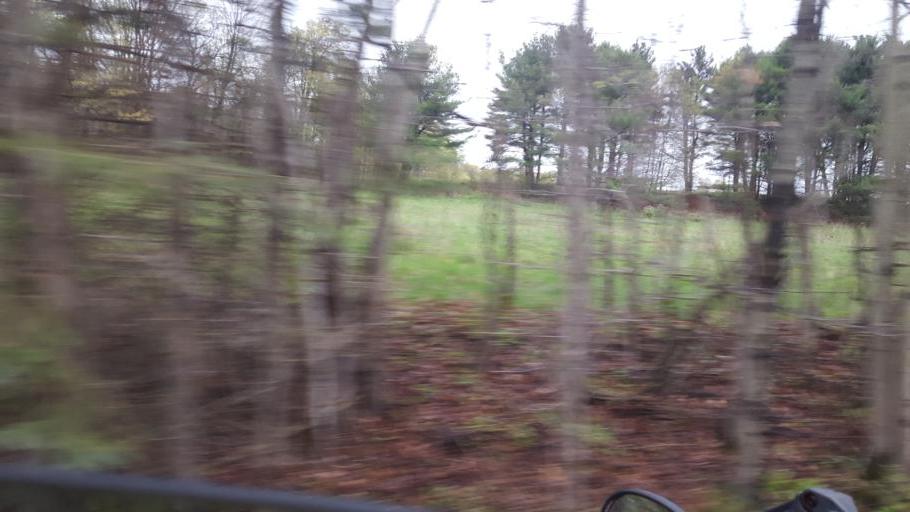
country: US
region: New York
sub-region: Allegany County
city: Andover
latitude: 41.9408
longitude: -77.7894
